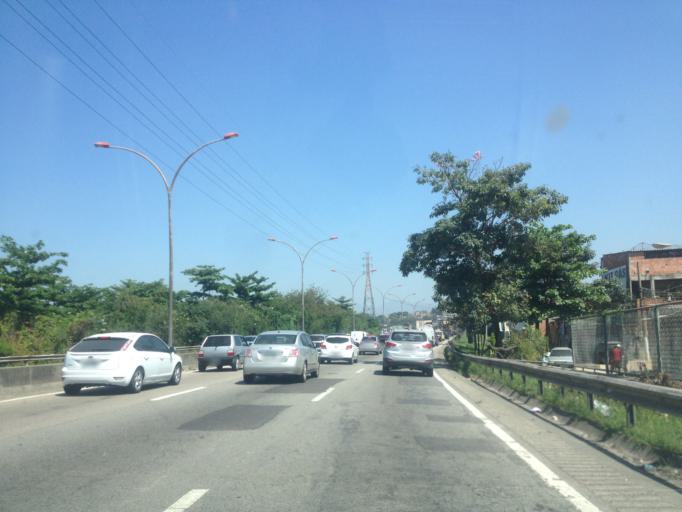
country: BR
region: Rio de Janeiro
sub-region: Duque De Caxias
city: Duque de Caxias
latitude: -22.8006
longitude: -43.3222
